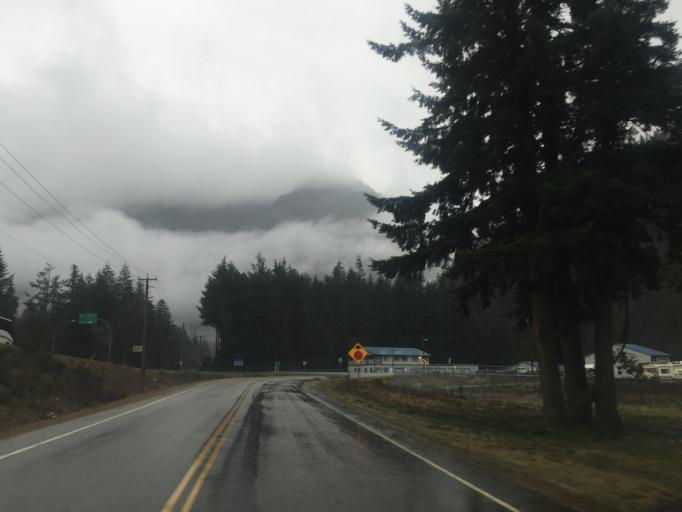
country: CA
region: British Columbia
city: Hope
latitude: 49.3642
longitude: -121.4777
